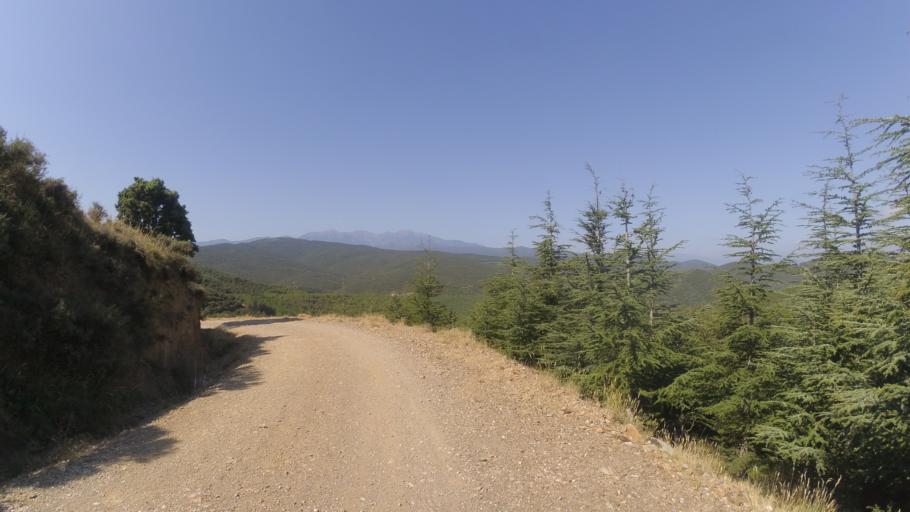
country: FR
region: Languedoc-Roussillon
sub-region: Departement des Pyrenees-Orientales
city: Millas
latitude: 42.6257
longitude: 2.6751
